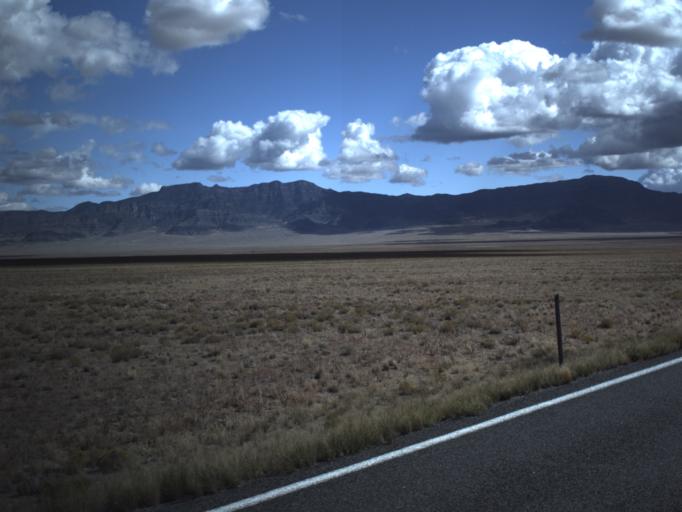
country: US
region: Utah
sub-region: Beaver County
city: Milford
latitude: 38.5576
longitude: -113.7504
